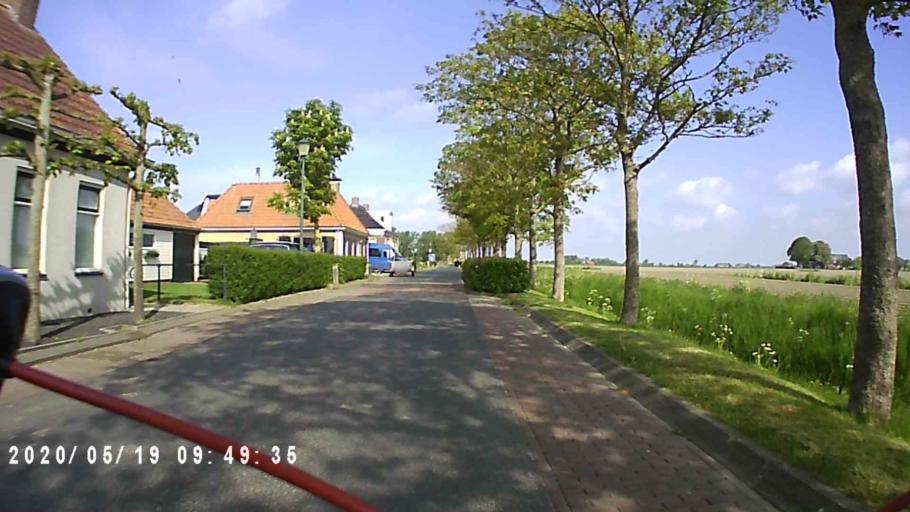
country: NL
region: Groningen
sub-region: Gemeente Zuidhorn
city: Grijpskerk
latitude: 53.2825
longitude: 6.2660
